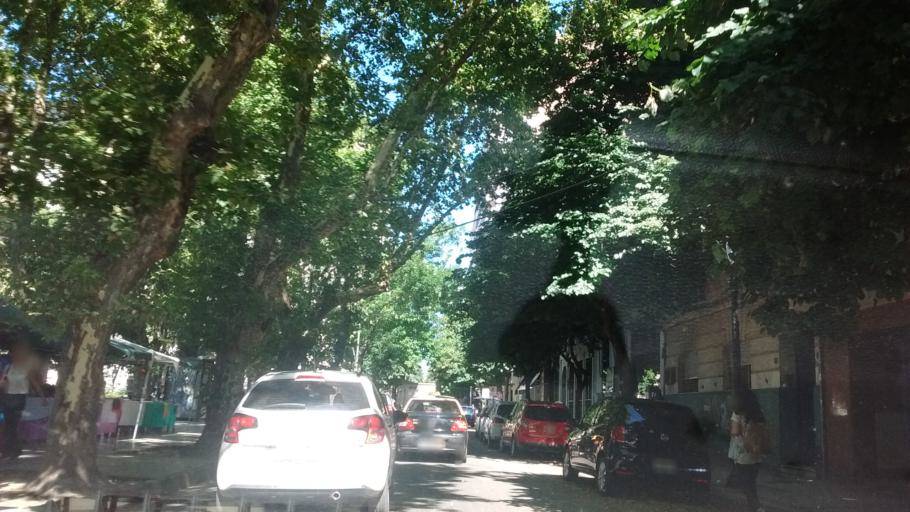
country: AR
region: Santa Fe
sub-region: Departamento de Rosario
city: Rosario
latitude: -32.9443
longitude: -60.6502
